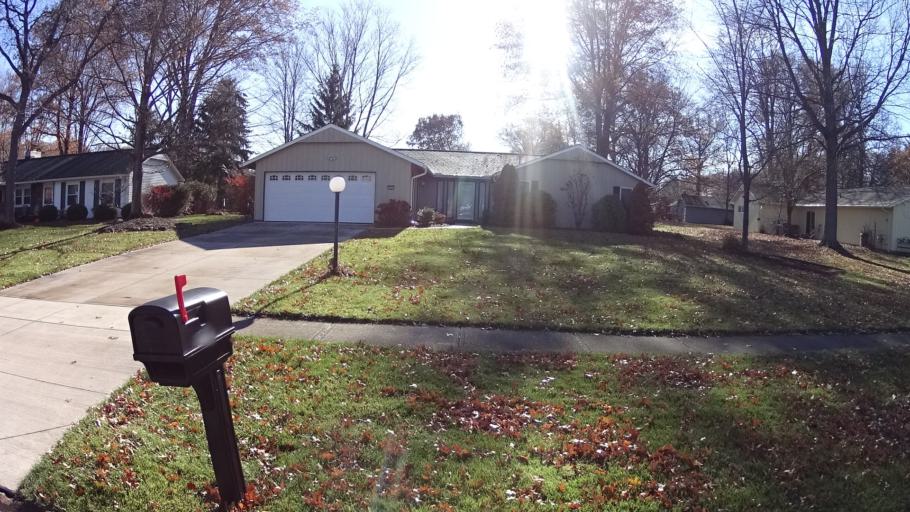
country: US
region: Ohio
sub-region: Lorain County
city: North Ridgeville
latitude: 41.4126
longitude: -81.9817
